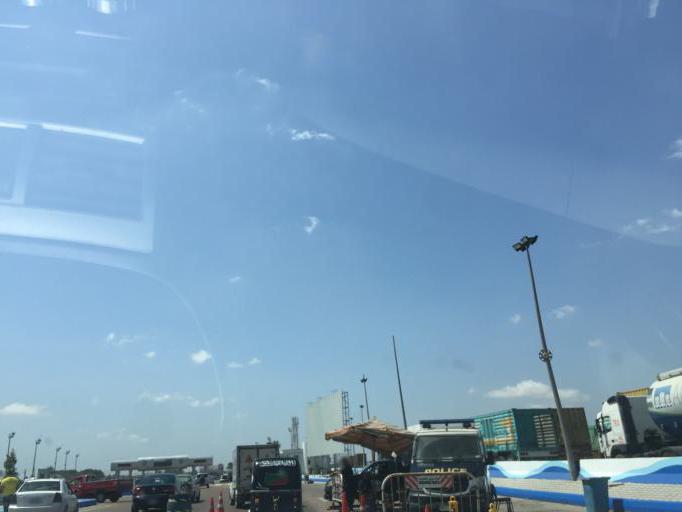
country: EG
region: Alexandria
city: Alexandria
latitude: 30.9676
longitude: 29.8296
